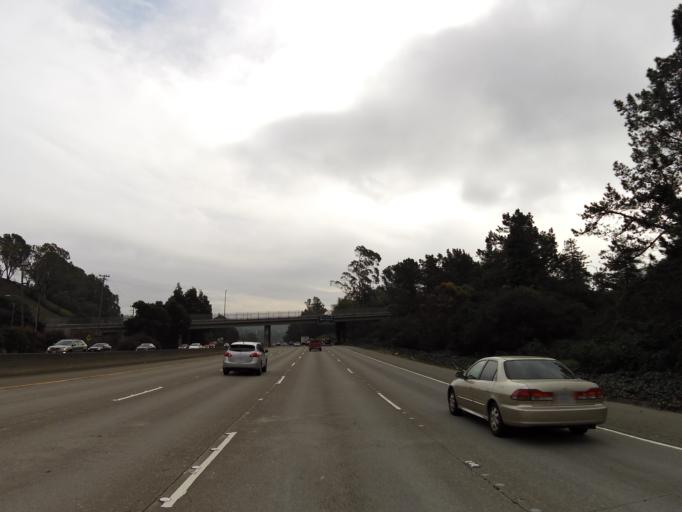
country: US
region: California
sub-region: Alameda County
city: San Leandro
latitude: 37.7674
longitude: -122.1532
